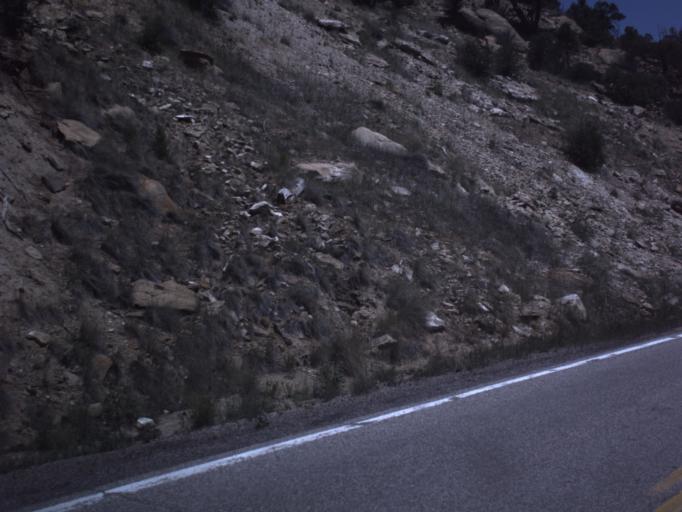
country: US
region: Utah
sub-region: Emery County
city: Orangeville
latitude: 39.2891
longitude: -111.2554
